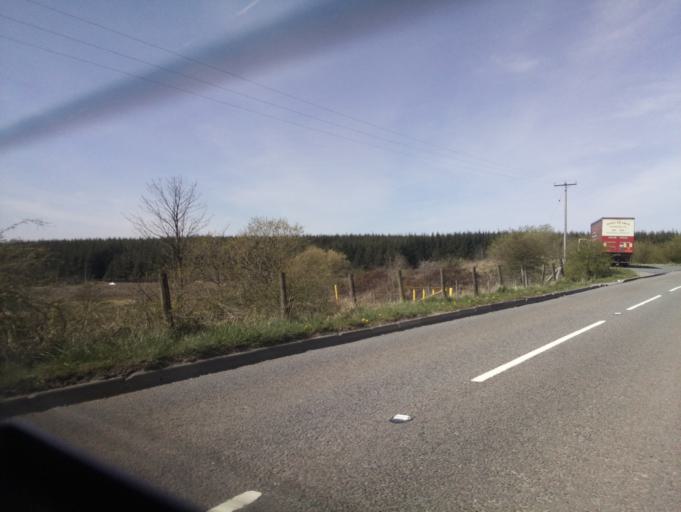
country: GB
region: Wales
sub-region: Rhondda Cynon Taf
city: Aberdare
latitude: 51.7527
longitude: -3.4436
